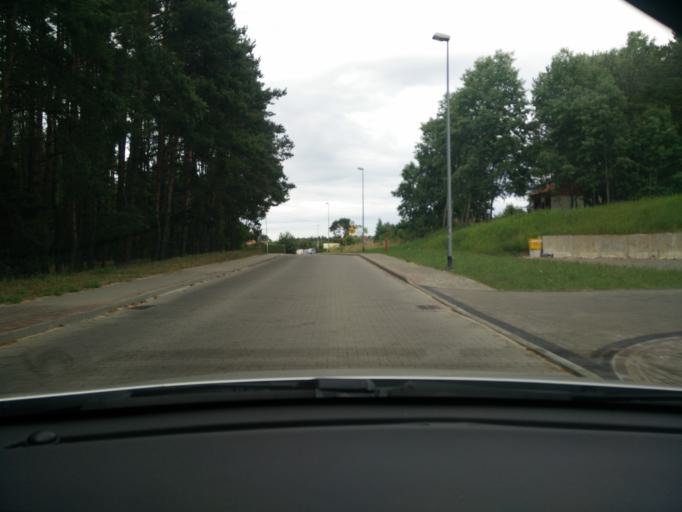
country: PL
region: Pomeranian Voivodeship
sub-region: Powiat pucki
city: Mosty
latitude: 54.6037
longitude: 18.4861
